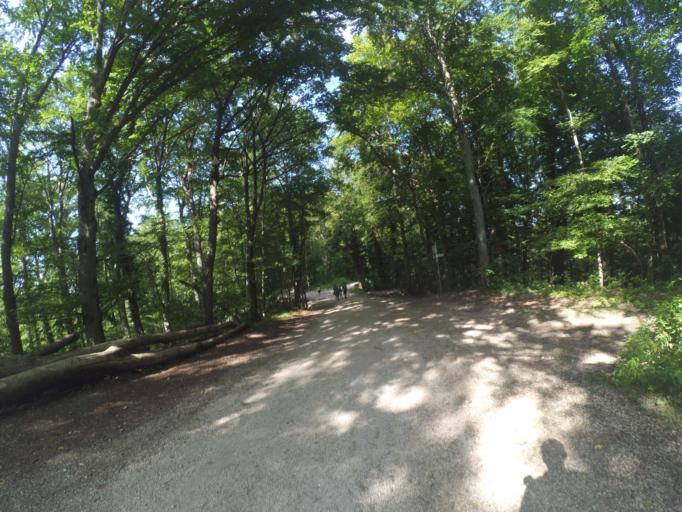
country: DE
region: Baden-Wuerttemberg
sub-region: Tuebingen Region
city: Bad Urach
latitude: 48.4885
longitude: 9.3775
